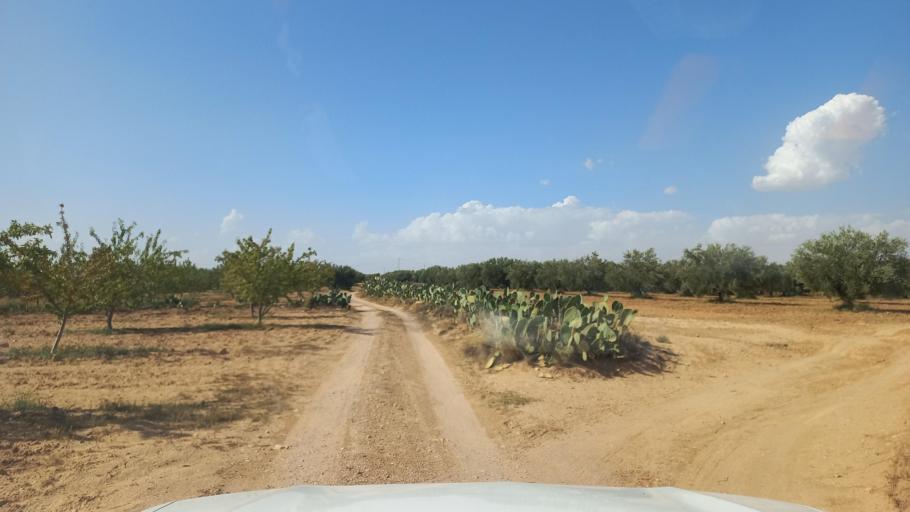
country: TN
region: Al Qasrayn
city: Kasserine
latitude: 35.2700
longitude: 9.0240
